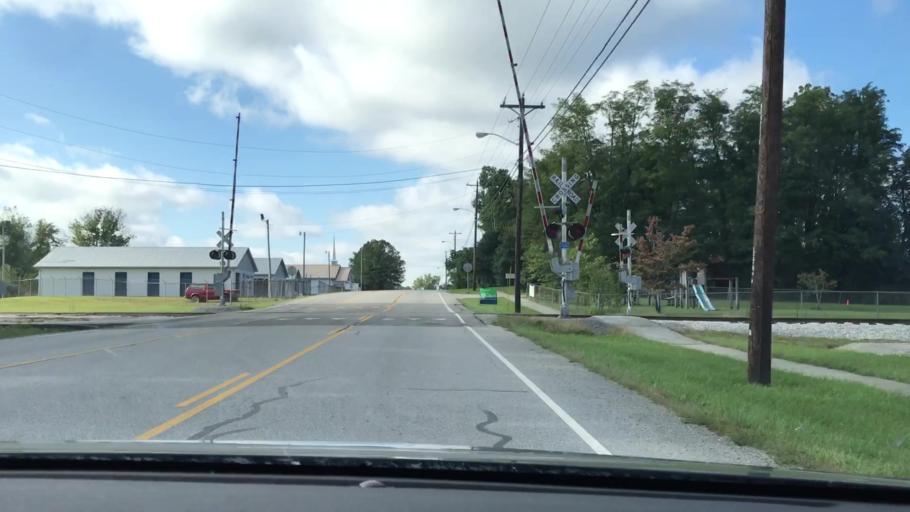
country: US
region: Tennessee
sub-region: Putnam County
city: Monterey
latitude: 36.1445
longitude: -85.2643
